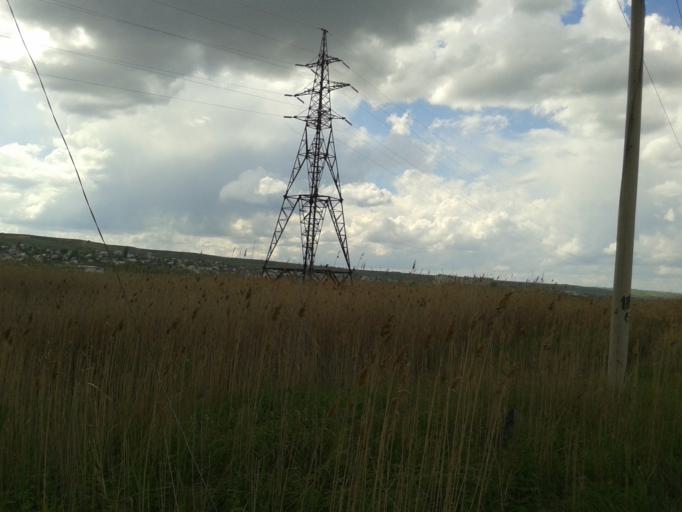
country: RU
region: Volgograd
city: Krasnoslobodsk
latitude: 48.5194
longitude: 44.5105
